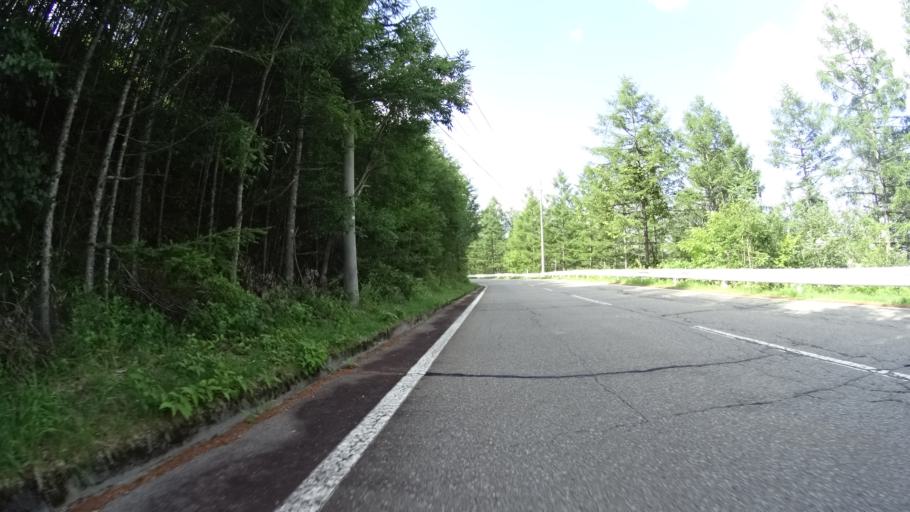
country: JP
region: Nagano
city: Saku
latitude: 36.0583
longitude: 138.3951
